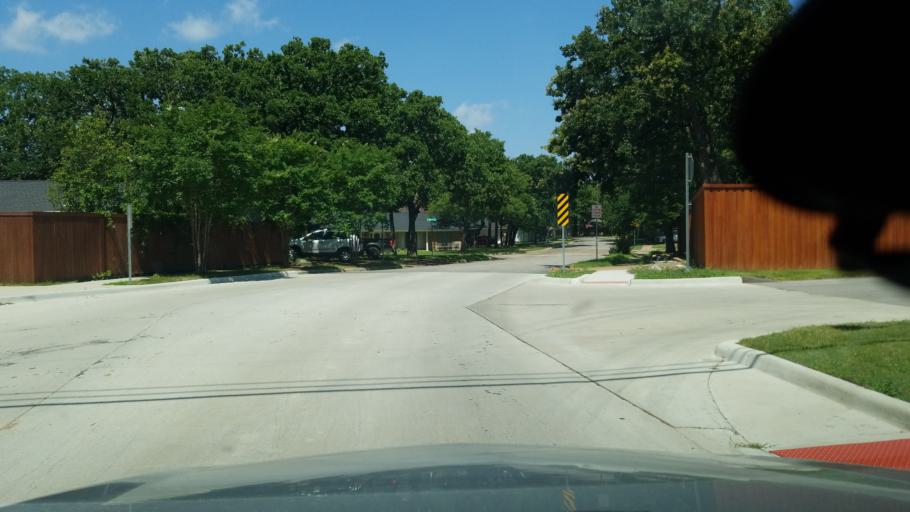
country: US
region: Texas
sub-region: Dallas County
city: Irving
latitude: 32.8334
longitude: -96.9526
